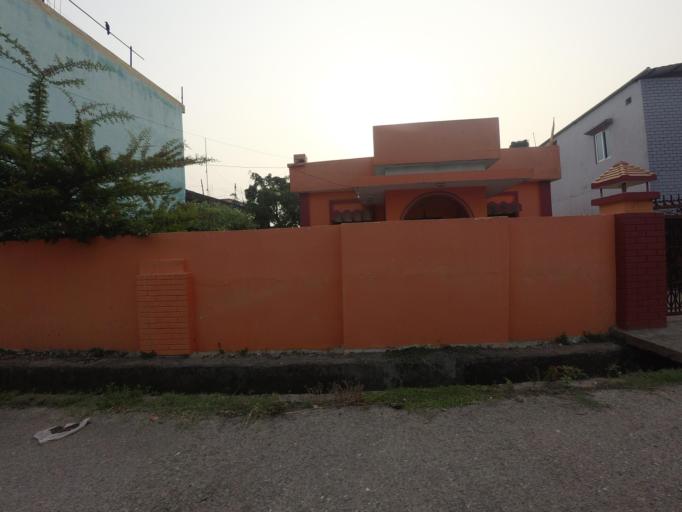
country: NP
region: Western Region
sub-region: Lumbini Zone
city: Bhairahawa
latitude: 27.5105
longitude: 83.4470
